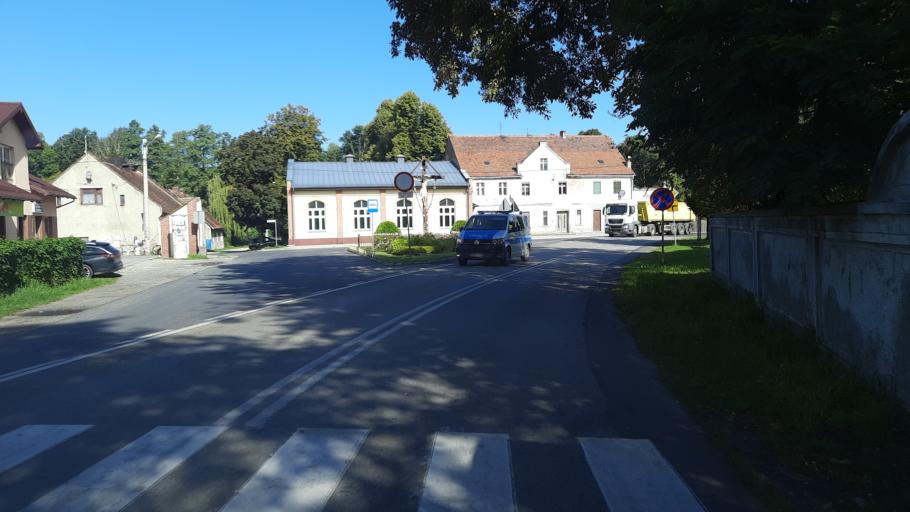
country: PL
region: Lower Silesian Voivodeship
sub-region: Powiat wroclawski
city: Dlugoleka
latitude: 51.1941
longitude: 17.1832
